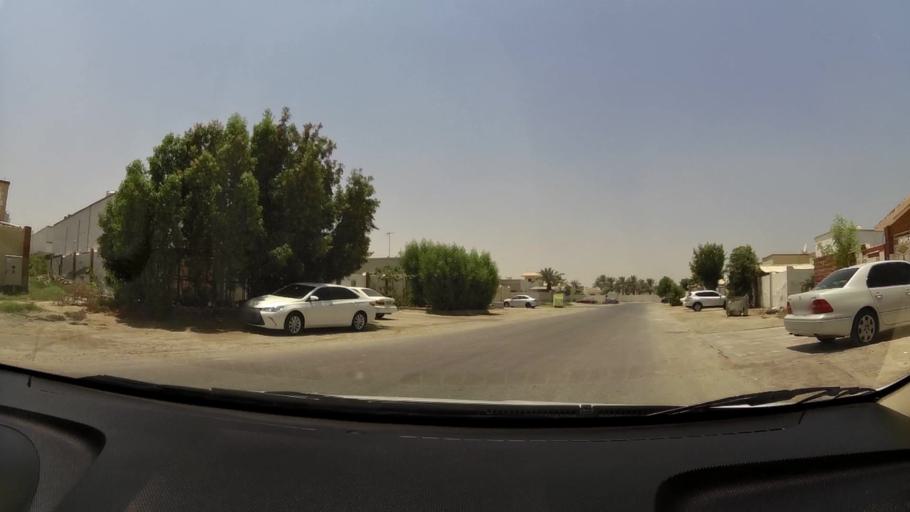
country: AE
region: Umm al Qaywayn
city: Umm al Qaywayn
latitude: 25.5488
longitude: 55.5486
